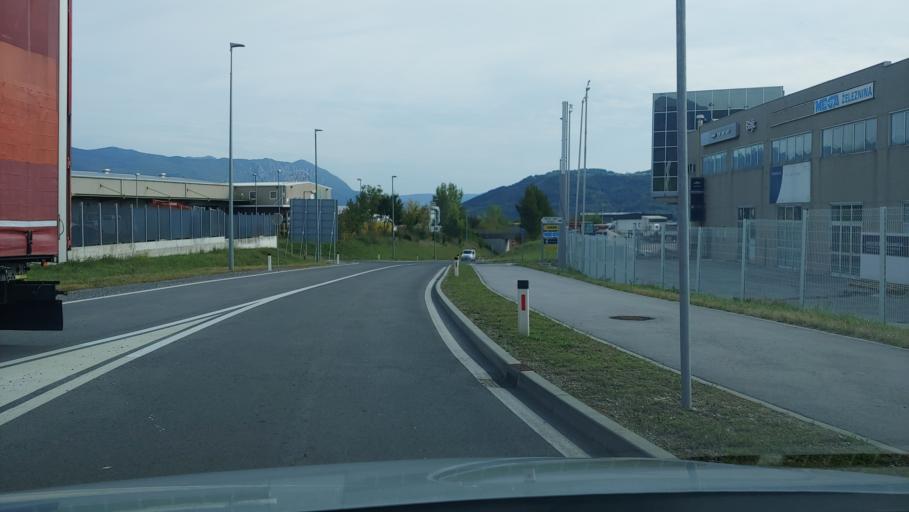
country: SI
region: Ajdovscina
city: Lokavec
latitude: 45.8862
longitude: 13.8901
